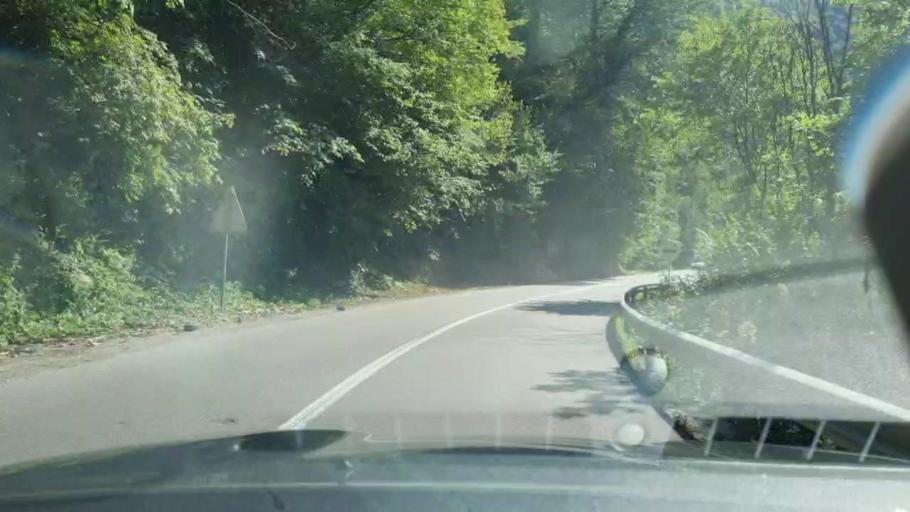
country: BA
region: Federation of Bosnia and Herzegovina
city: Bosanska Krupa
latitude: 44.8666
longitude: 16.0957
